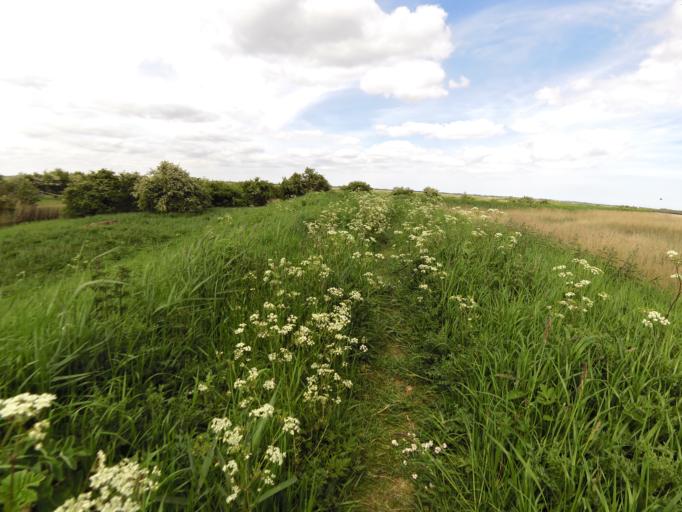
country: GB
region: England
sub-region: Norfolk
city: Gorleston-on-Sea
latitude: 52.5900
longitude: 1.6443
